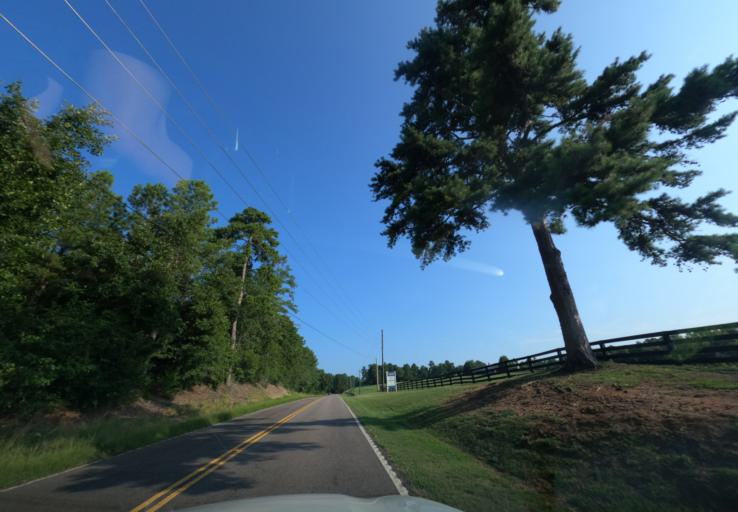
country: US
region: South Carolina
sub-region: Edgefield County
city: Murphys Estates
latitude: 33.6666
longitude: -81.9765
